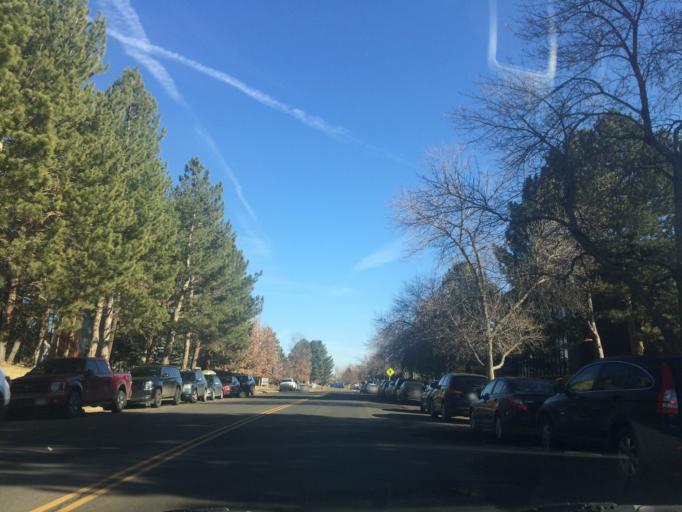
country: US
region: Colorado
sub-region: Boulder County
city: Boulder
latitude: 40.0254
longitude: -105.2207
